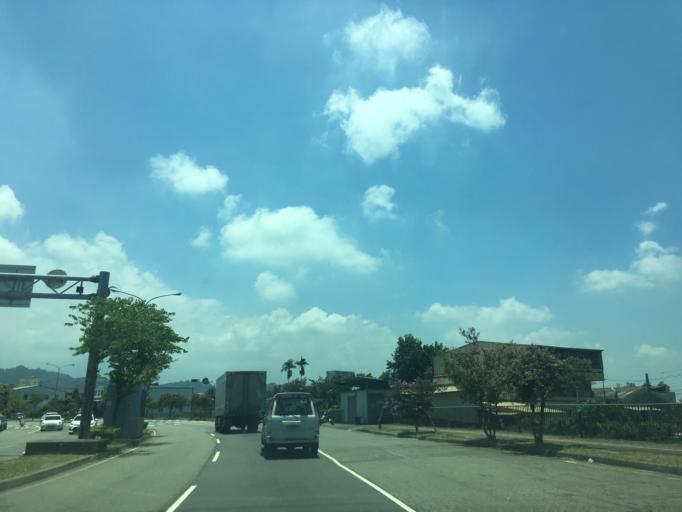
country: TW
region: Taiwan
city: Fengyuan
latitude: 24.2378
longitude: 120.7036
